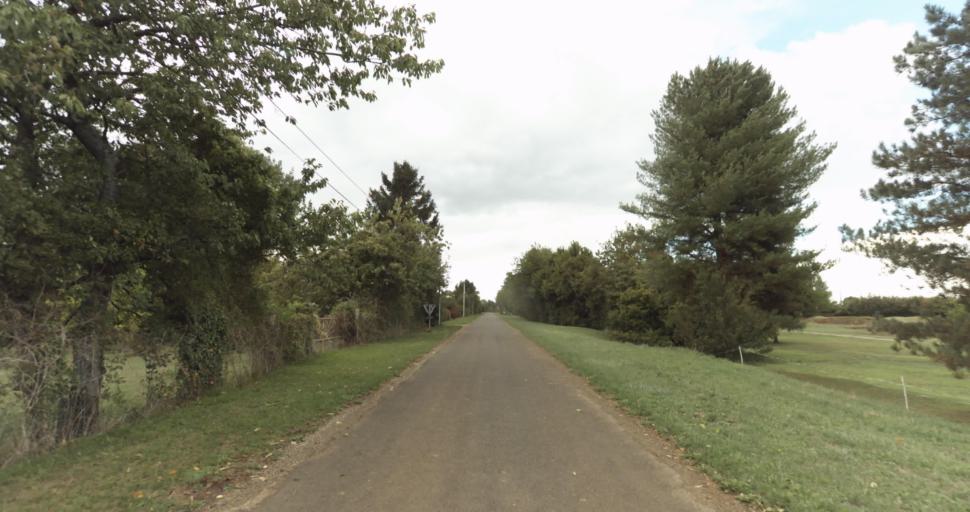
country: FR
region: Lower Normandy
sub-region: Departement de l'Orne
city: Sainte-Gauburge-Sainte-Colombe
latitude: 48.7294
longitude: 0.3947
